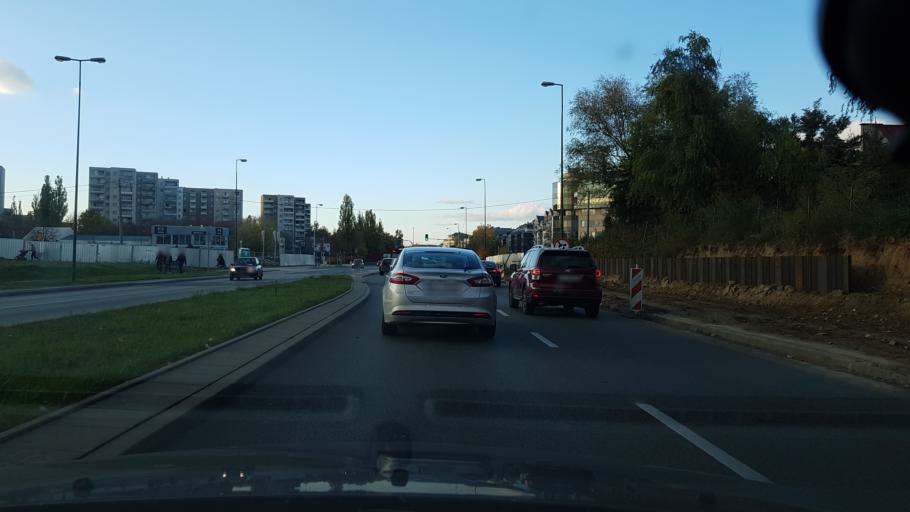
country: PL
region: Masovian Voivodeship
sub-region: Warszawa
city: Ursynow
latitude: 52.1481
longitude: 21.0609
